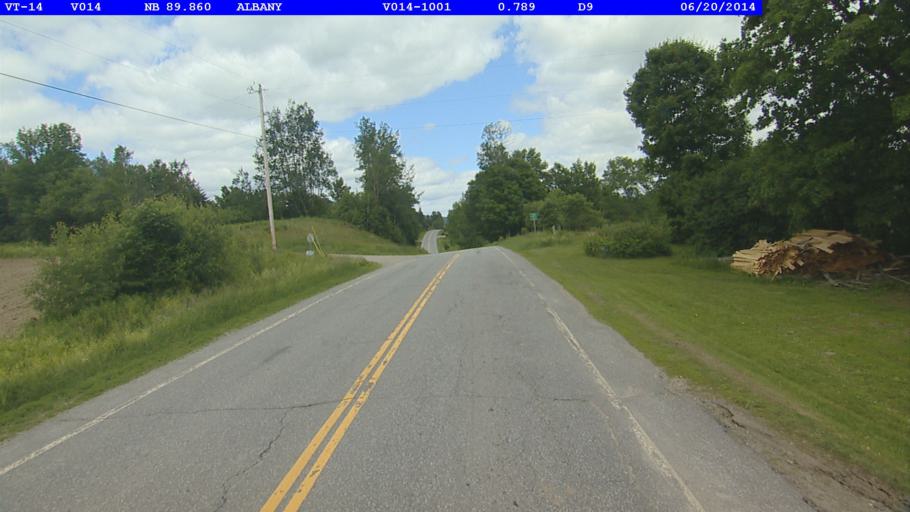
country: US
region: Vermont
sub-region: Caledonia County
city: Hardwick
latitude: 44.7137
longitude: -72.3880
